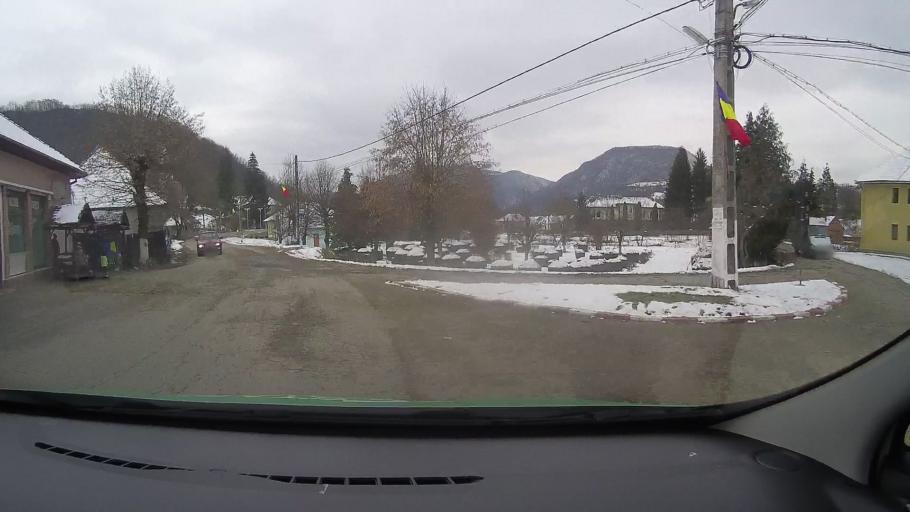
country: RO
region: Hunedoara
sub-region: Comuna Balsa
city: Balsa
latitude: 46.0285
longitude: 23.0998
